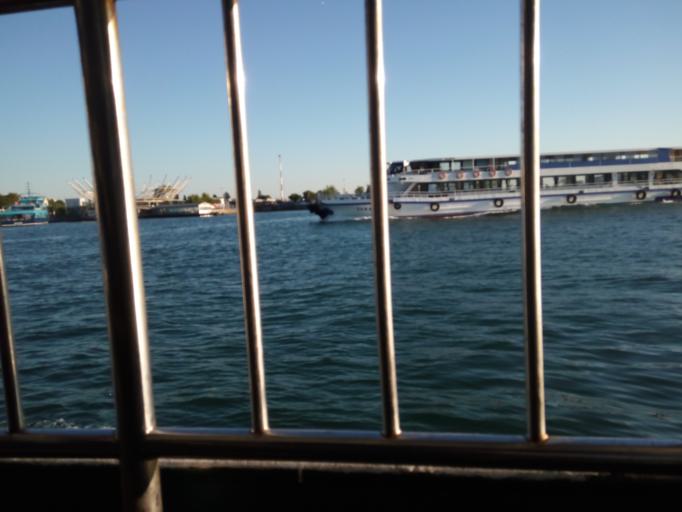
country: TR
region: Istanbul
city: UEskuedar
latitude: 40.9930
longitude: 29.0190
